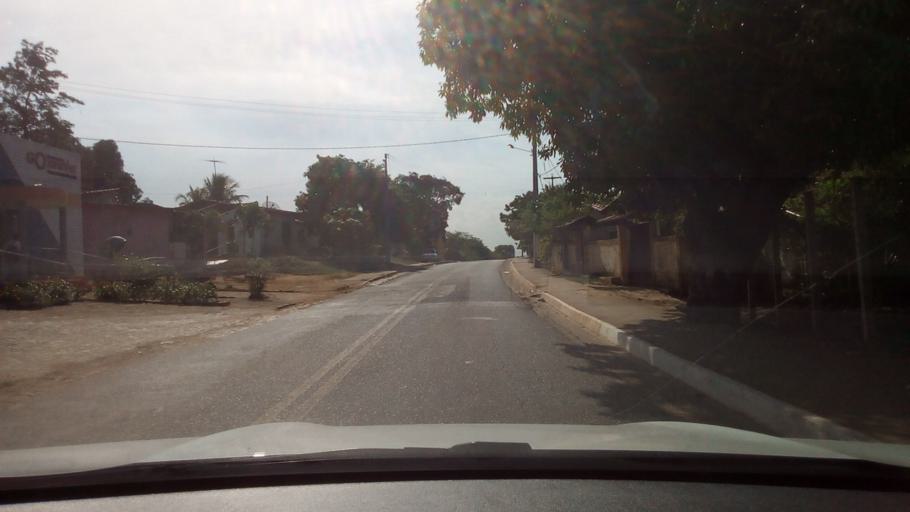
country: BR
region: Rio Grande do Norte
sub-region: Ares
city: Ares
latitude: -6.2342
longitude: -35.1544
